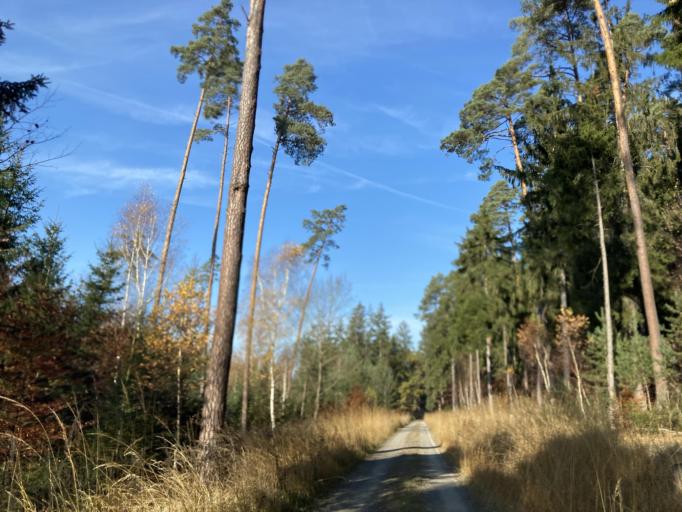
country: DE
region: Baden-Wuerttemberg
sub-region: Regierungsbezirk Stuttgart
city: Altdorf
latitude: 48.5759
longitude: 9.0028
